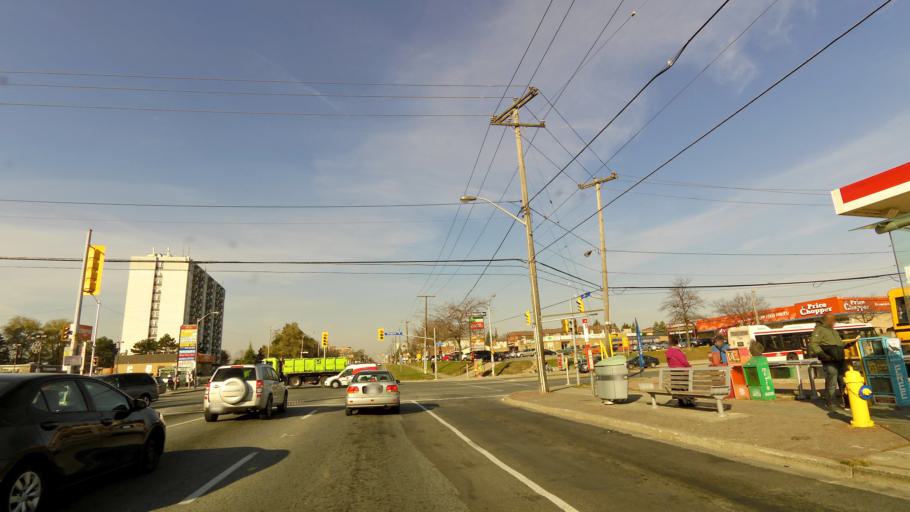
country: CA
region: Ontario
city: Concord
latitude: 43.7391
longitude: -79.5130
